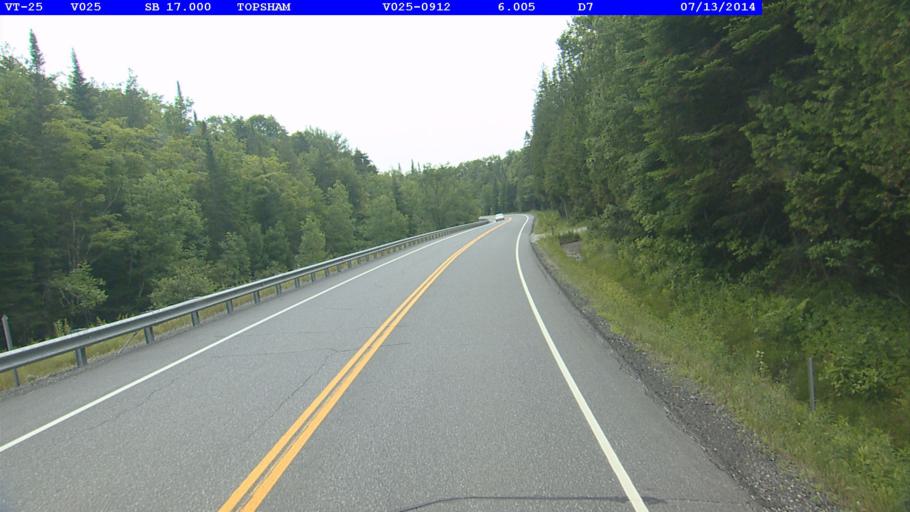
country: US
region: Vermont
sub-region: Orange County
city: Chelsea
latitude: 44.1315
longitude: -72.3134
